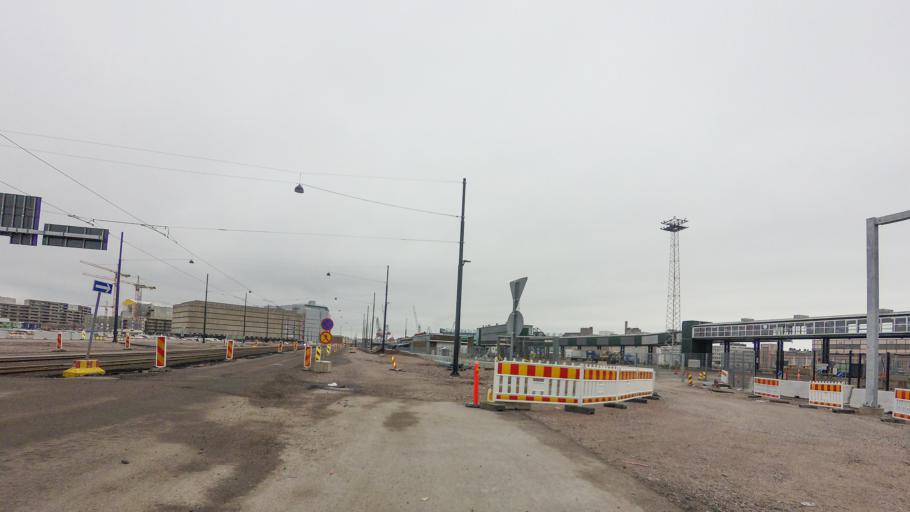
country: FI
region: Uusimaa
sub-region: Helsinki
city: Helsinki
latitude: 60.1524
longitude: 24.9176
